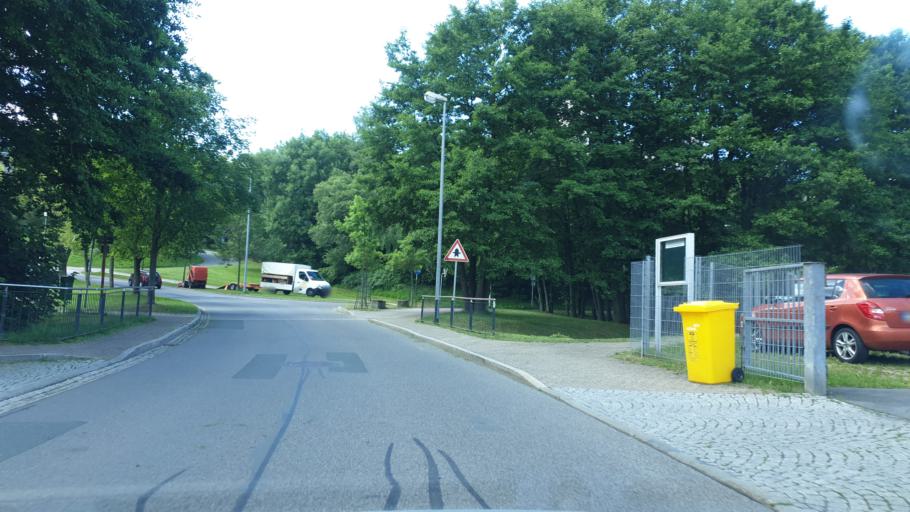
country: DE
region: Saxony
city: Marienberg
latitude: 50.6494
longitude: 13.1496
